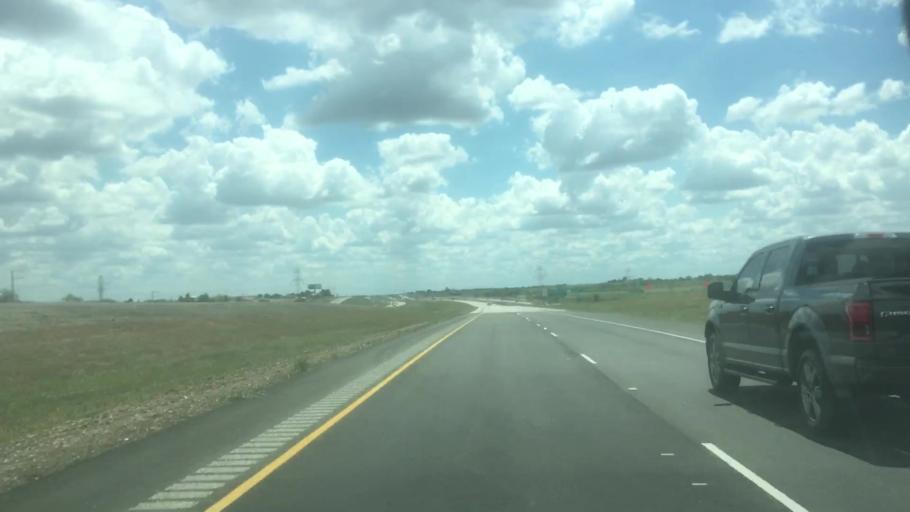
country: US
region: Texas
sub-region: Caldwell County
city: Uhland
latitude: 30.0036
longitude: -97.6873
